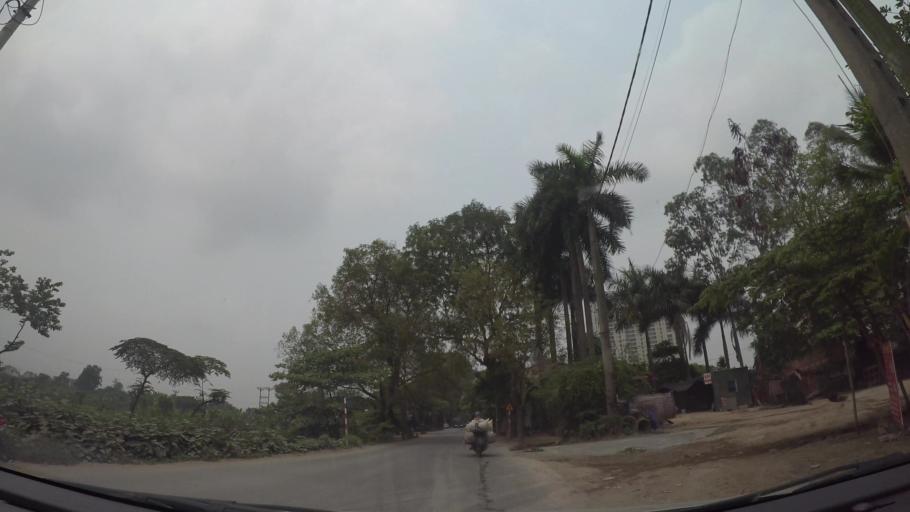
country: VN
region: Ha Noi
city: Cau Dien
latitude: 21.0140
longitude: 105.7461
